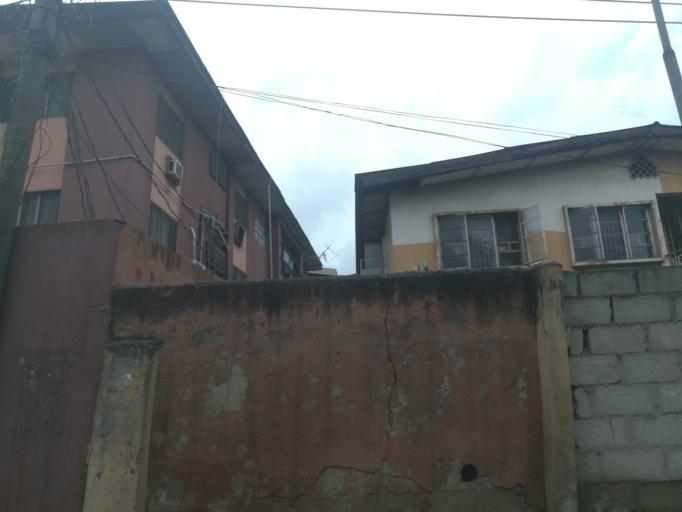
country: NG
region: Lagos
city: Somolu
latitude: 6.5333
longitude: 3.3896
